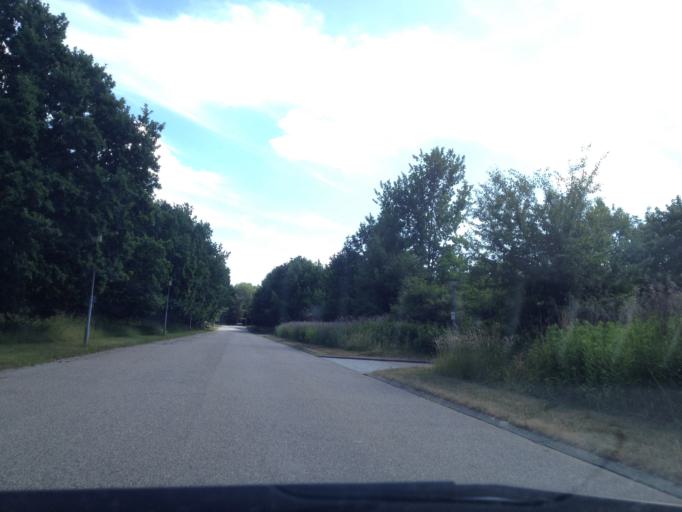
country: DK
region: Capital Region
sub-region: Horsholm Kommune
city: Horsholm
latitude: 55.8703
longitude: 12.4930
